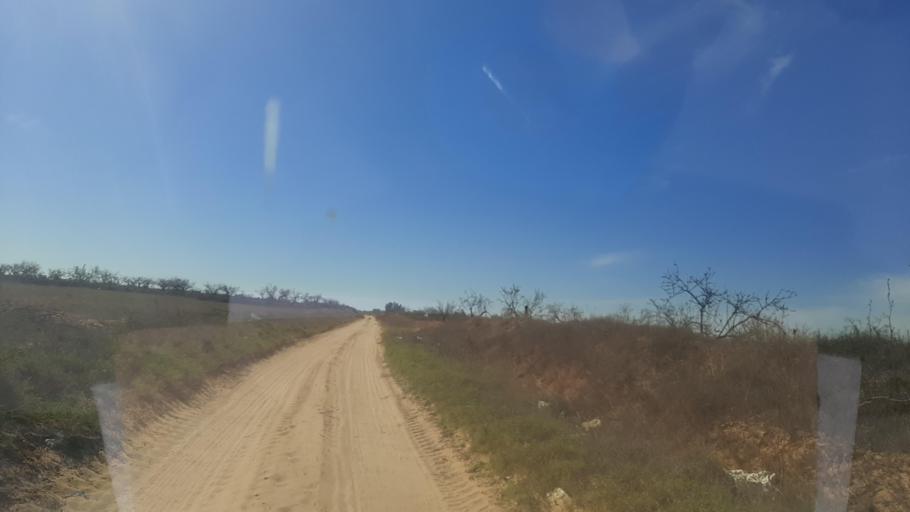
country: TN
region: Safaqis
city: Sfax
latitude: 34.8286
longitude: 10.5556
